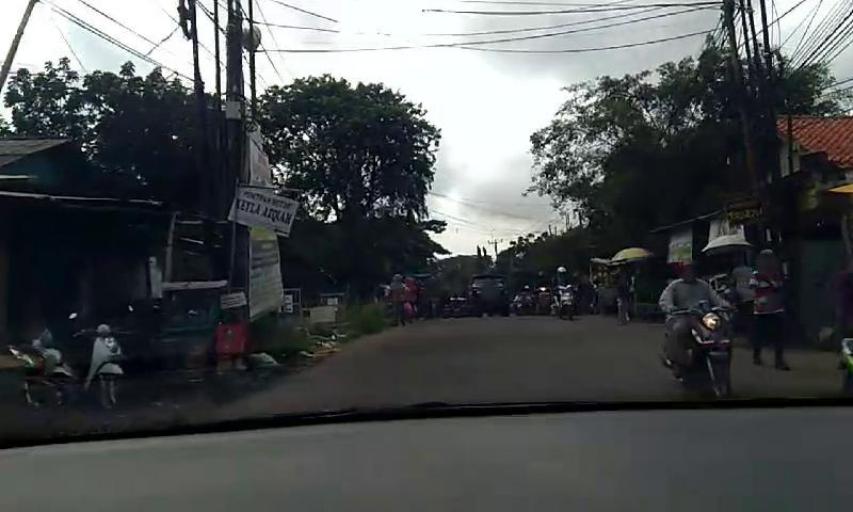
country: ID
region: West Java
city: Bekasi
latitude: -6.1977
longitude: 106.9855
